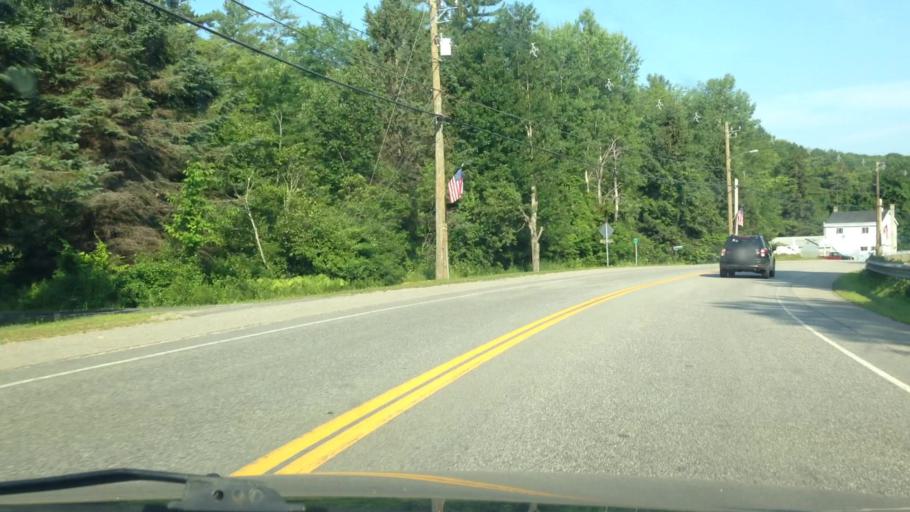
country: US
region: New Hampshire
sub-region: Cheshire County
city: Marlborough
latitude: 42.9102
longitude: -72.2200
